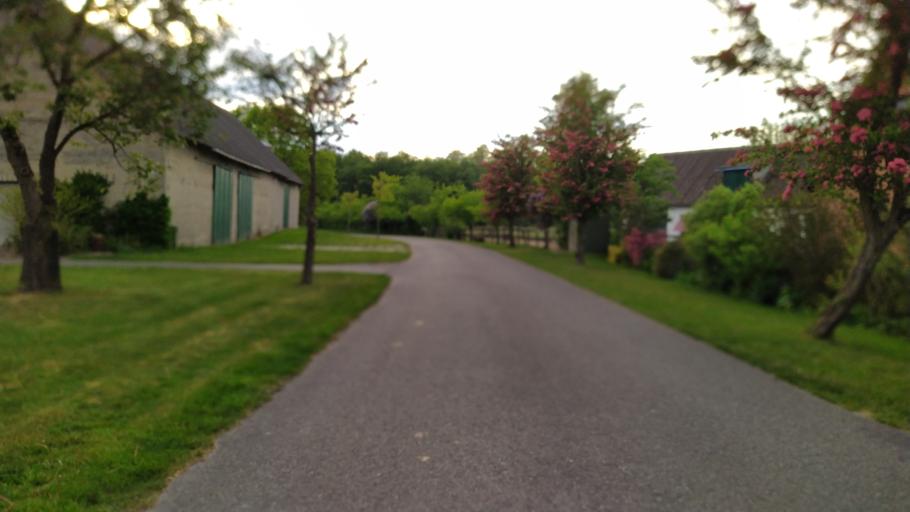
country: DE
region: Lower Saxony
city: Ahlerstedt
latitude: 53.3520
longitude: 9.4013
